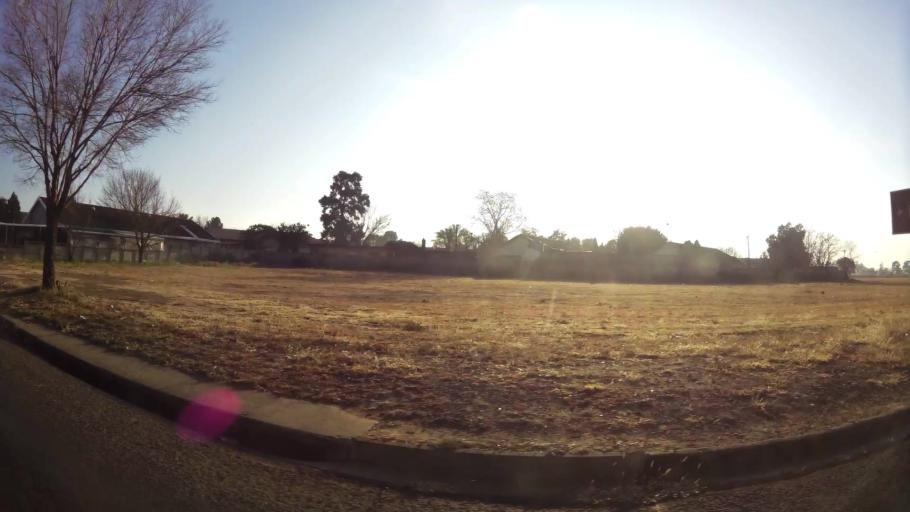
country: ZA
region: Orange Free State
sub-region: Mangaung Metropolitan Municipality
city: Bloemfontein
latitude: -29.1690
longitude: 26.1955
